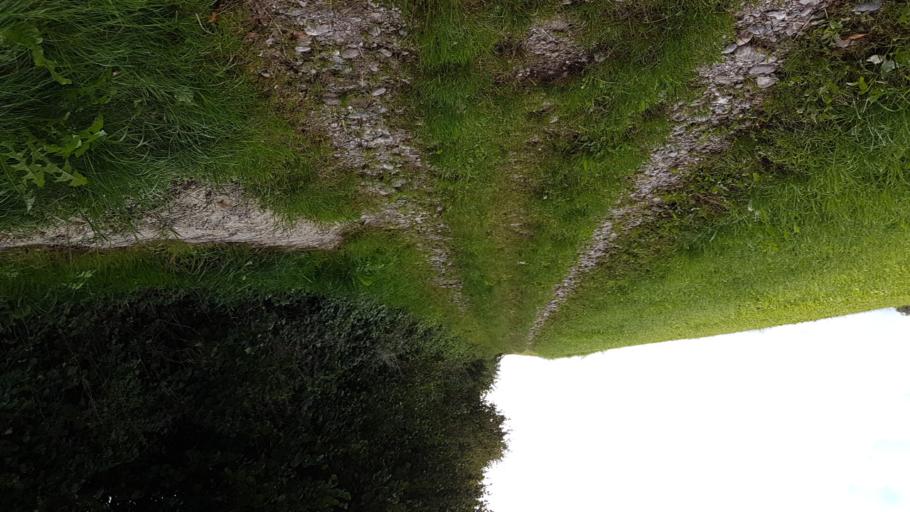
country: CH
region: Bern
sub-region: Bern-Mittelland District
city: Konolfingen
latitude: 46.8729
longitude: 7.6043
